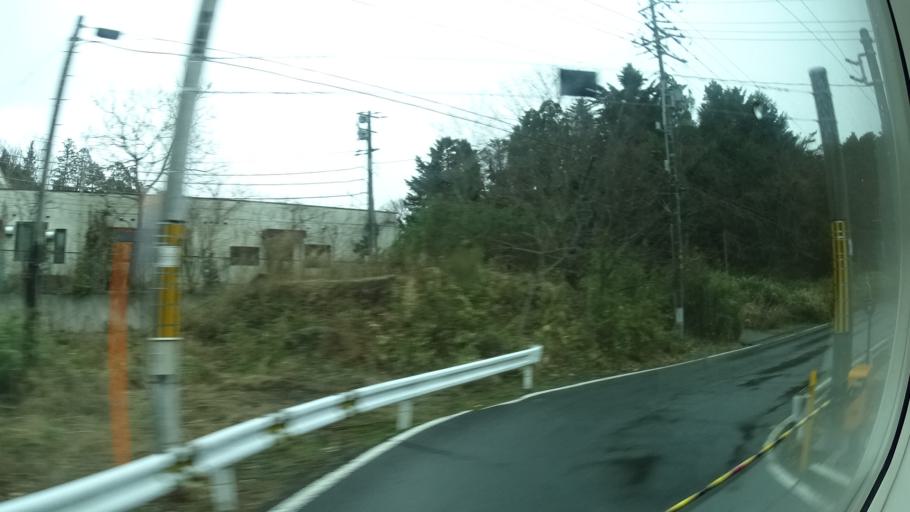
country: JP
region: Fukushima
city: Namie
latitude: 37.4607
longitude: 141.0094
